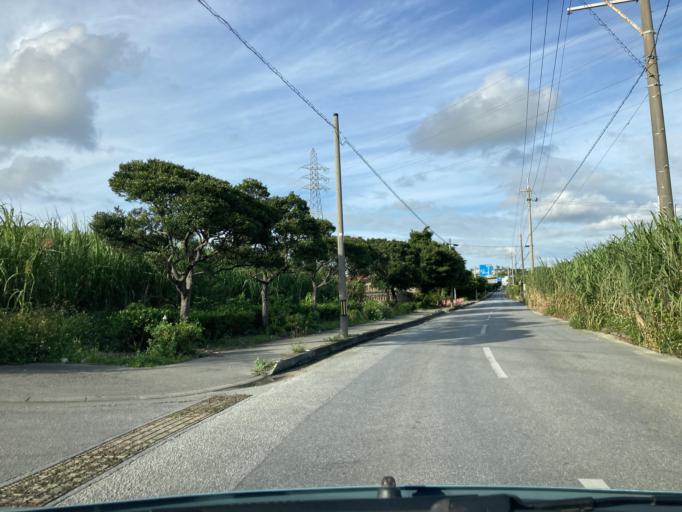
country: JP
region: Okinawa
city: Itoman
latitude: 26.1367
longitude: 127.7463
